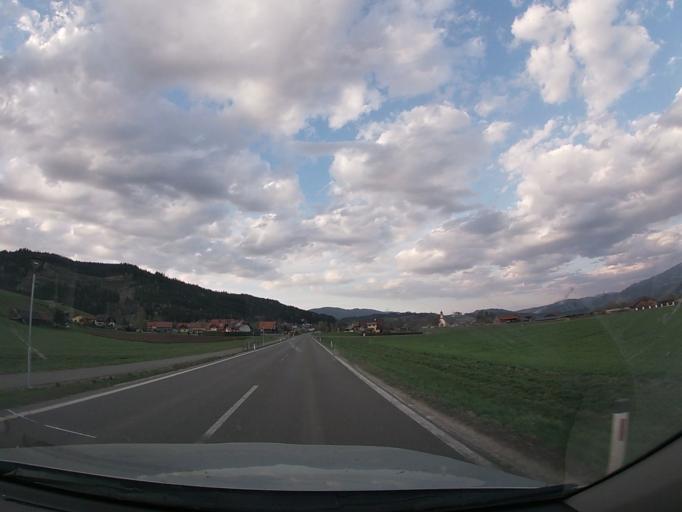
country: AT
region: Styria
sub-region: Politischer Bezirk Murtal
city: Knittelfeld
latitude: 47.2332
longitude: 14.8307
